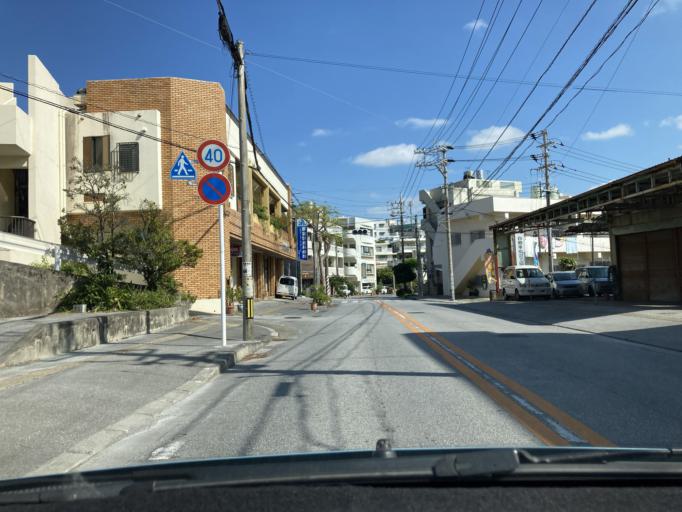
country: JP
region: Okinawa
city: Tomigusuku
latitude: 26.1941
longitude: 127.6726
